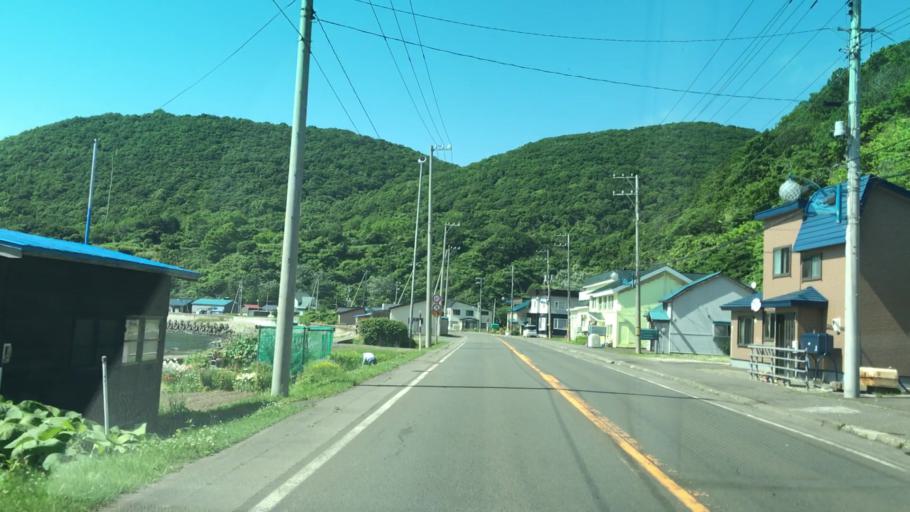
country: JP
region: Hokkaido
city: Iwanai
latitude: 43.1038
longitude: 140.4599
